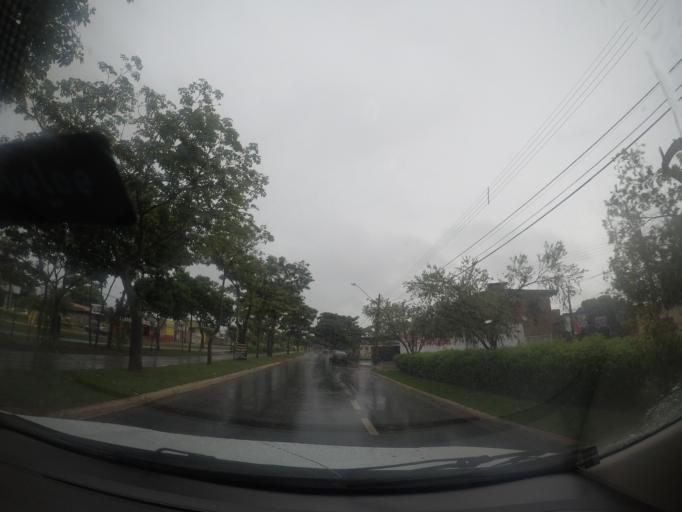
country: BR
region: Goias
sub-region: Goiania
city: Goiania
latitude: -16.6043
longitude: -49.3378
